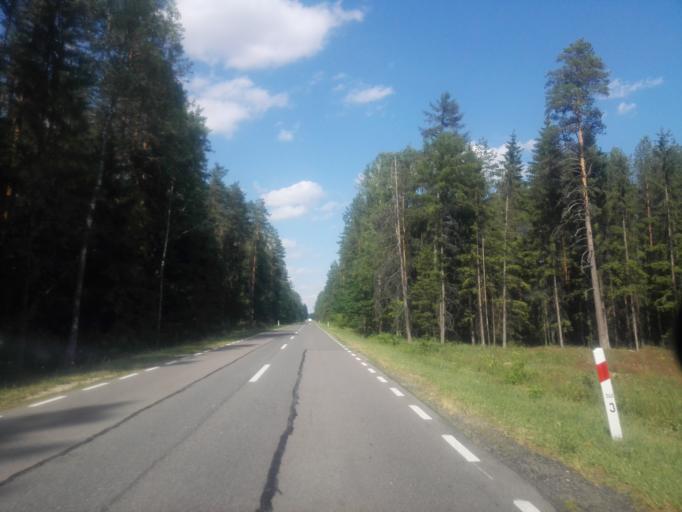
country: PL
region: Podlasie
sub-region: Powiat sejnenski
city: Sejny
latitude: 53.9875
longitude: 23.3007
